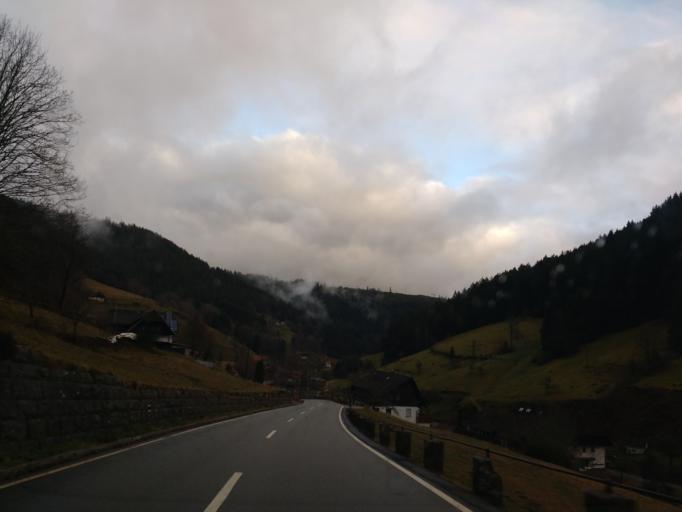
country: DE
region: Baden-Wuerttemberg
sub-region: Karlsruhe Region
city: Bad Rippoldsau-Schapbach
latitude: 48.4479
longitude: 8.2962
